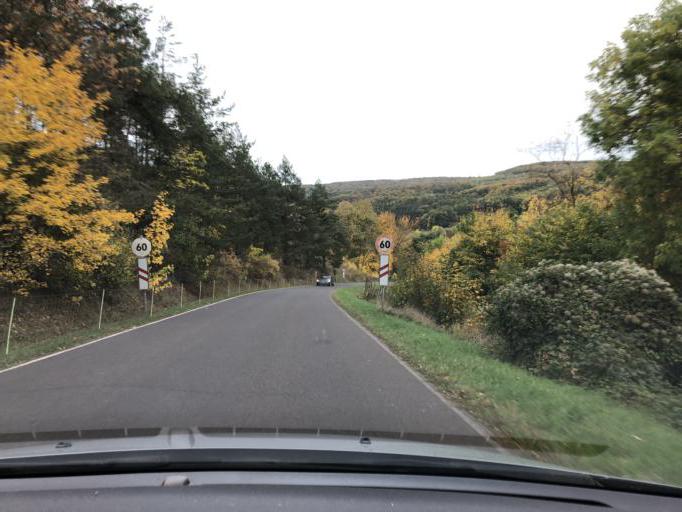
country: DE
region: Thuringia
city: Hetschburg
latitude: 50.9146
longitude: 11.2968
